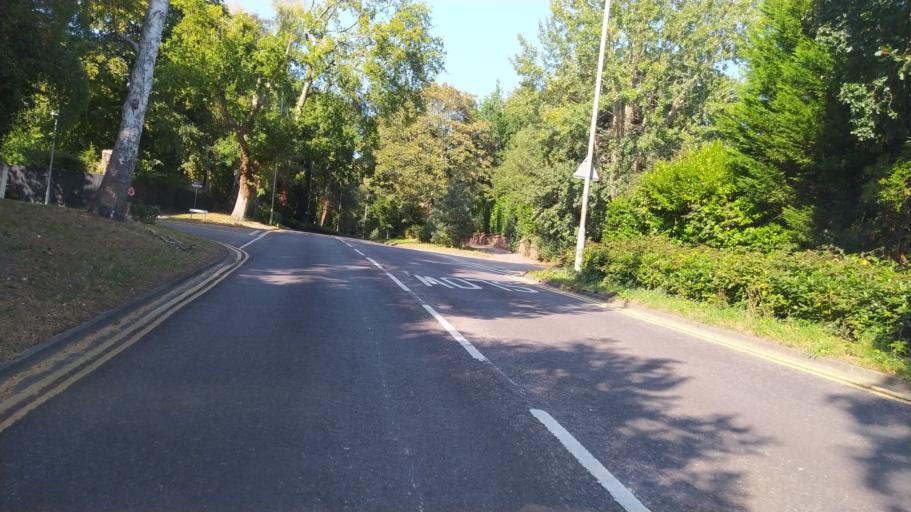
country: GB
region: England
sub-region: Bournemouth
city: Bournemouth
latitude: 50.7103
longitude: -1.9093
